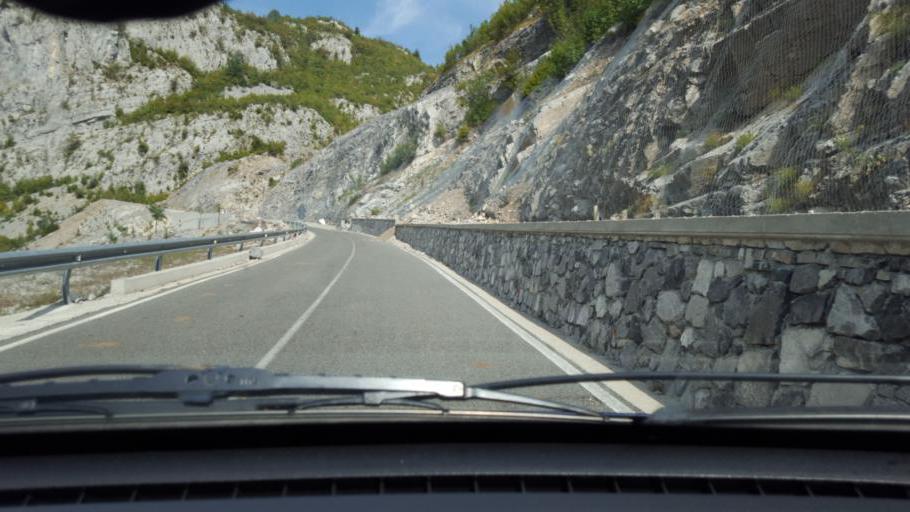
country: AL
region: Shkoder
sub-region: Rrethi i Malesia e Madhe
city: Kastrat
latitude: 42.5224
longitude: 19.6314
